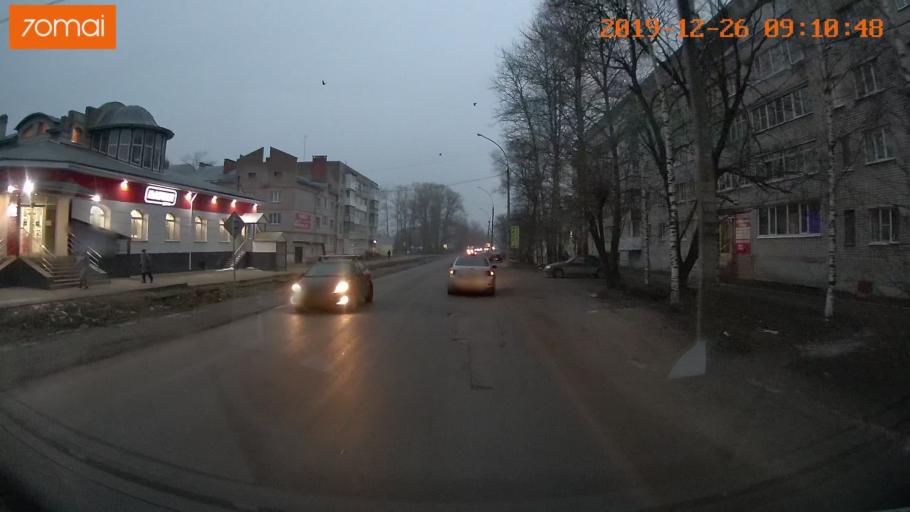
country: RU
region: Vologda
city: Gryazovets
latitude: 58.8729
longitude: 40.2525
